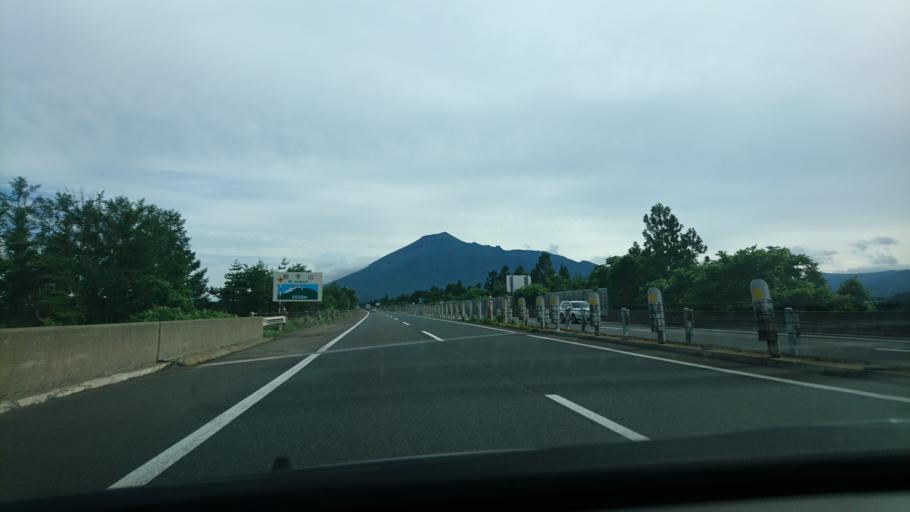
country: JP
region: Iwate
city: Shizukuishi
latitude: 39.9448
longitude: 141.0315
